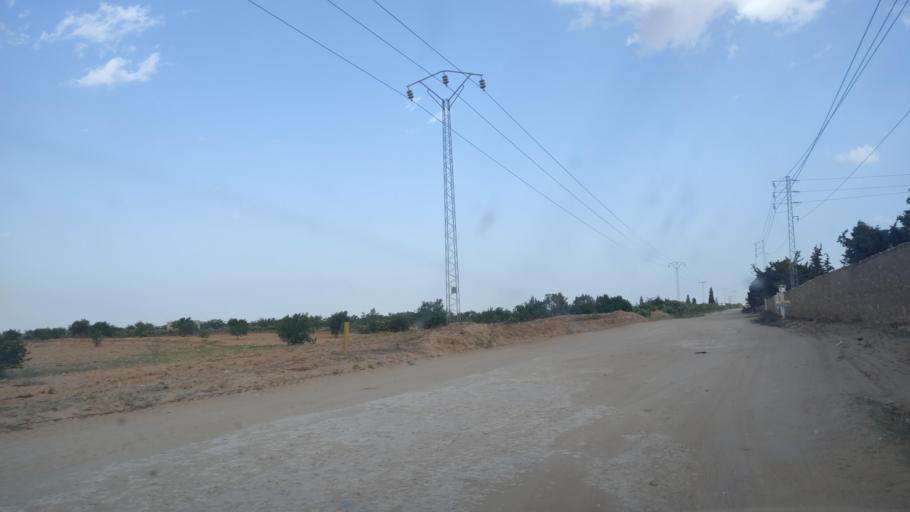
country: TN
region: Safaqis
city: Sfax
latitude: 34.8594
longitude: 10.6016
